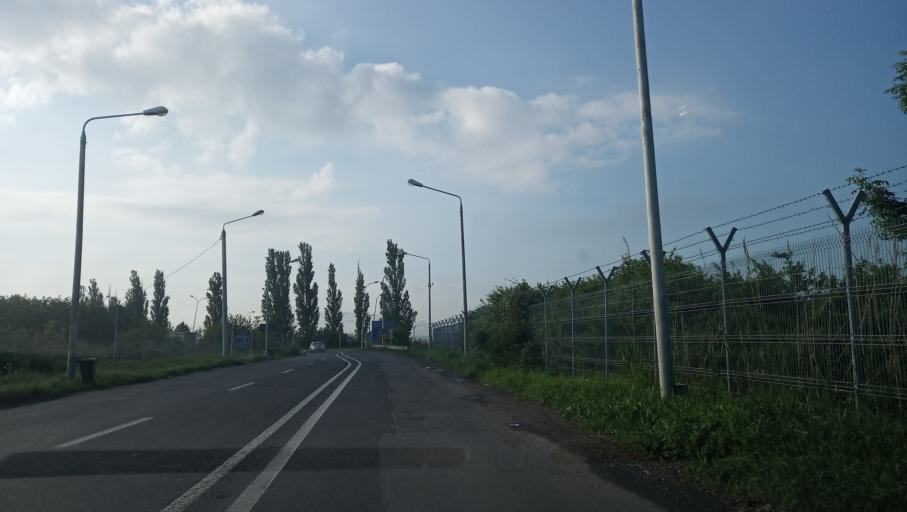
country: RO
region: Timis
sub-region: Comuna Moravita
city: Moravita
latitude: 45.2302
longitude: 21.2744
